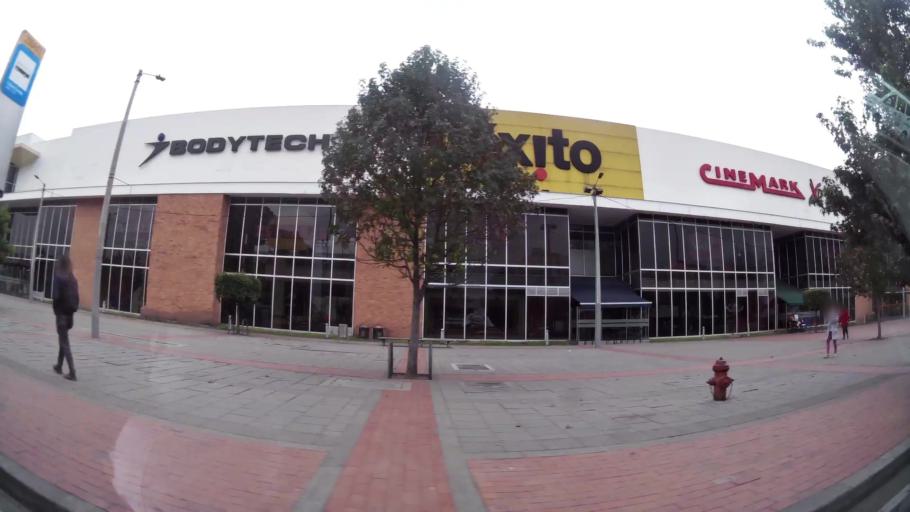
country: CO
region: Bogota D.C.
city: Barrio San Luis
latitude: 4.6873
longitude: -74.0746
